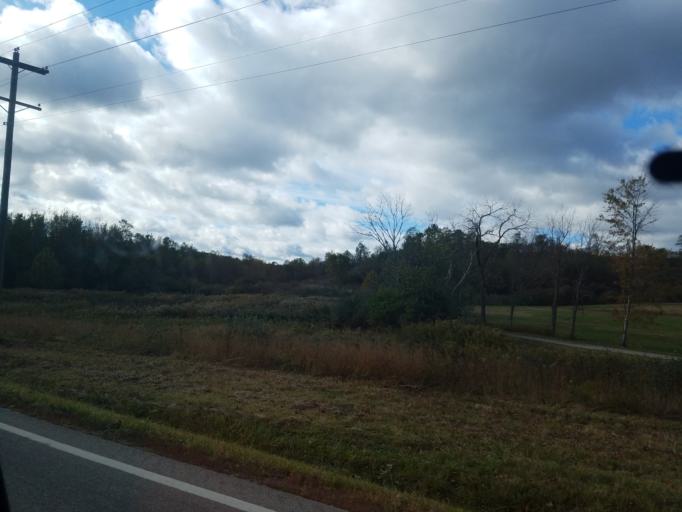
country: US
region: Ohio
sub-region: Vinton County
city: McArthur
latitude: 39.1925
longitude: -82.4764
